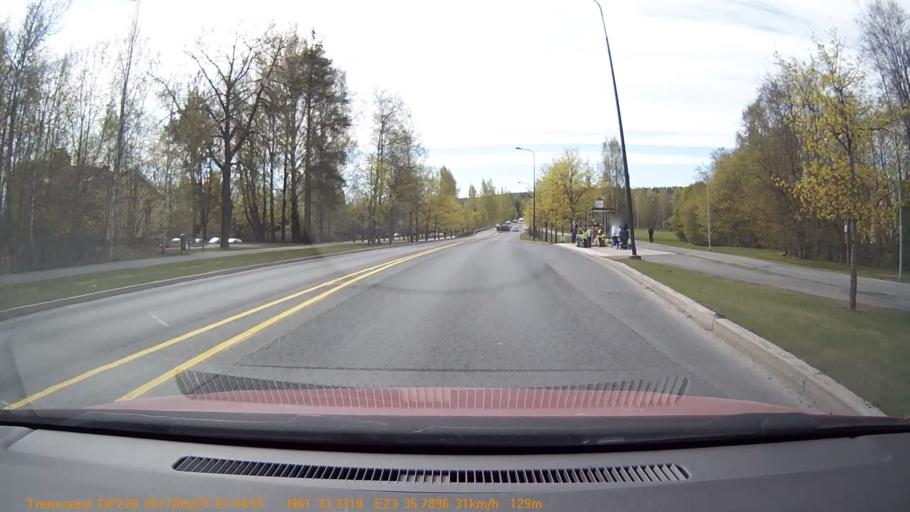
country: FI
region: Pirkanmaa
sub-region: Tampere
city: Yloejaervi
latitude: 61.5558
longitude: 23.5963
